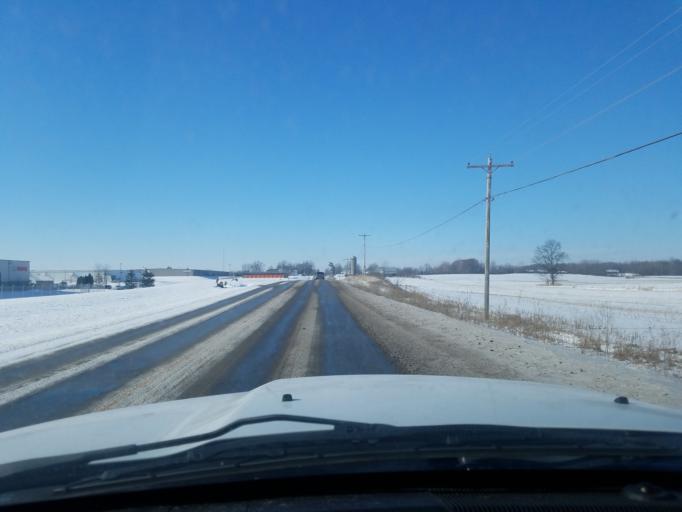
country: US
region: Indiana
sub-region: Noble County
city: Albion
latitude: 41.3960
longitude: -85.3986
